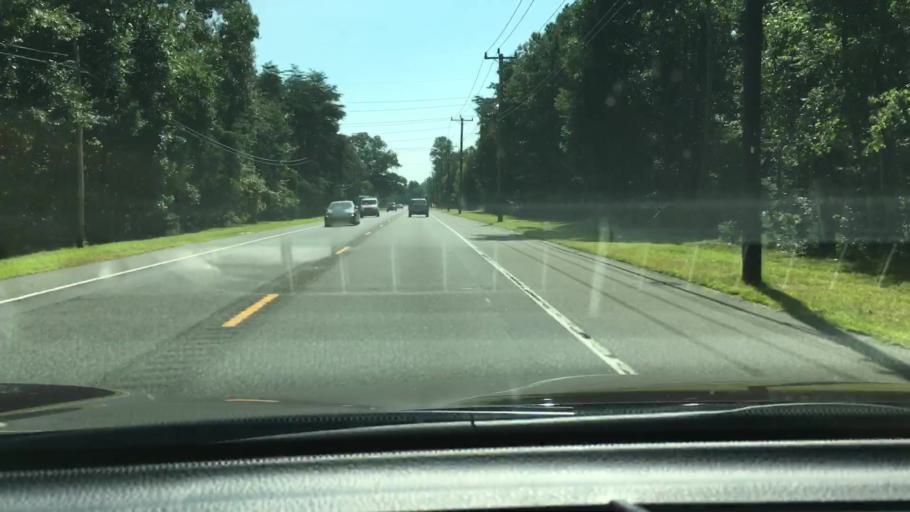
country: US
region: New Jersey
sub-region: Cumberland County
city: Laurel Lake
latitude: 39.3755
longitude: -74.9516
